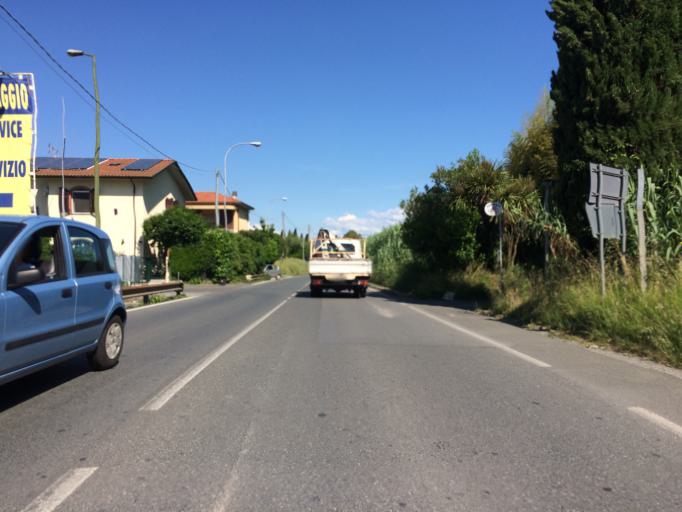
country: IT
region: Tuscany
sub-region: Provincia di Massa-Carrara
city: Borghetto-Melara
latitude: 44.0985
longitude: 9.9844
